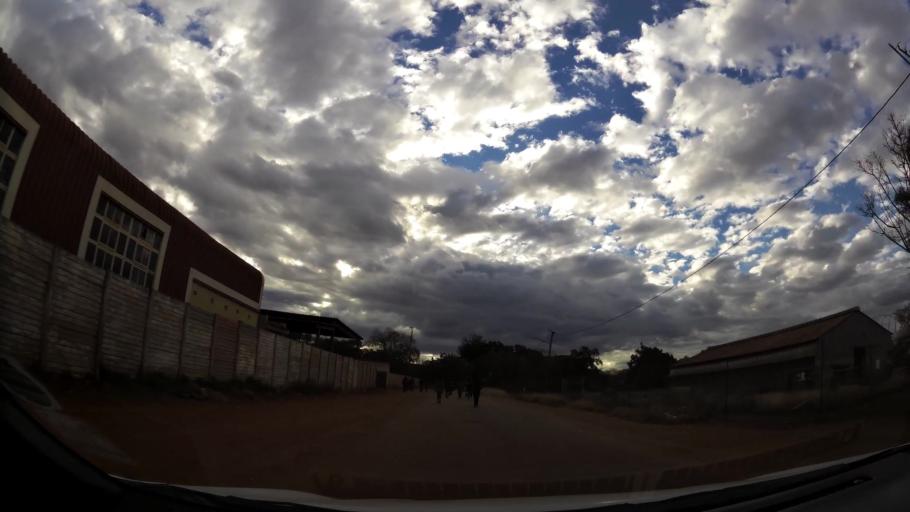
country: ZA
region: Limpopo
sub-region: Waterberg District Municipality
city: Modimolle
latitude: -24.5213
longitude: 28.7155
